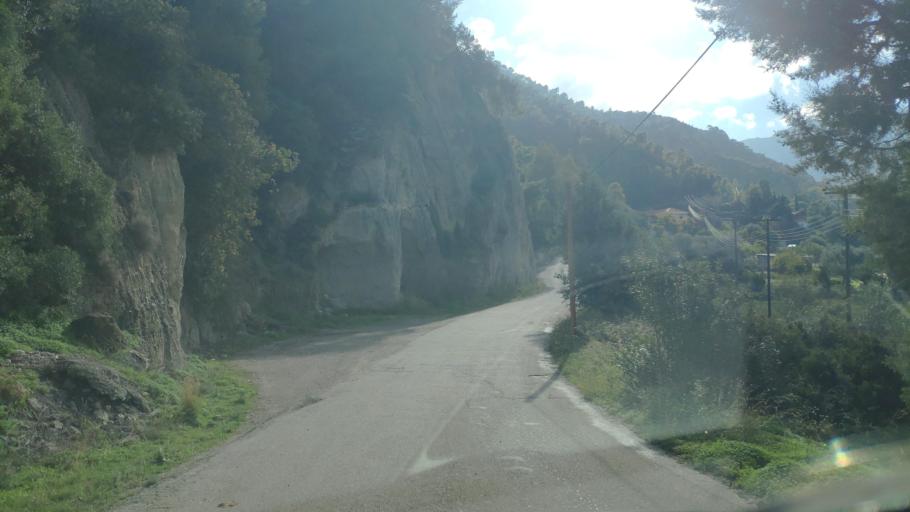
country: GR
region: West Greece
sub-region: Nomos Achaias
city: Aiyira
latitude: 38.1283
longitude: 22.4339
